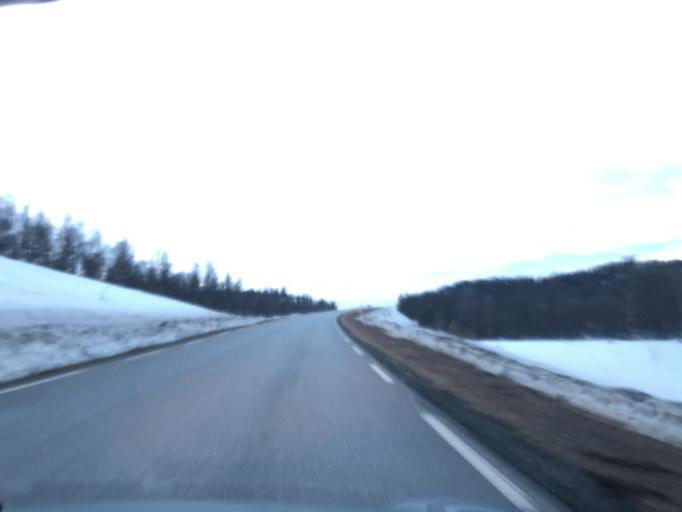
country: NO
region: Sor-Trondelag
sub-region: Tydal
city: Aas
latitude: 62.7390
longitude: 11.8323
